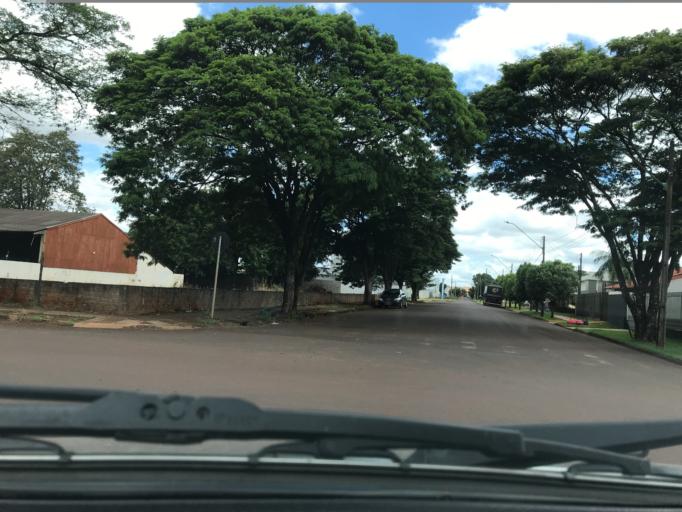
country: BR
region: Parana
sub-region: Palotina
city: Palotina
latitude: -24.2898
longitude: -53.8392
